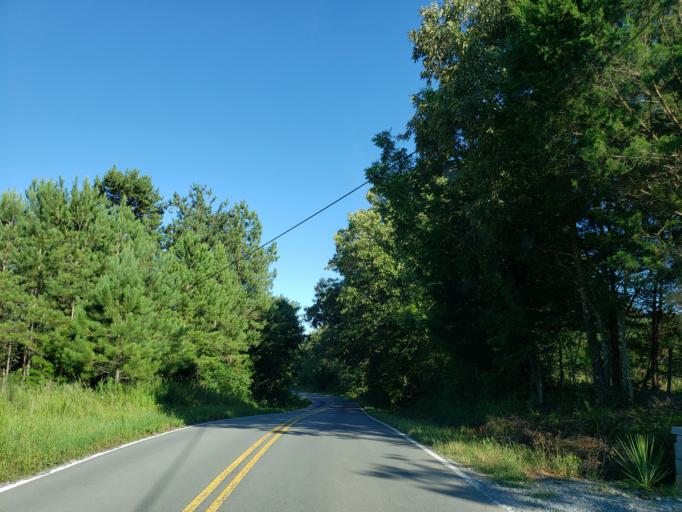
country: US
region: Georgia
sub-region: Polk County
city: Aragon
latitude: 34.1111
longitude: -85.0318
